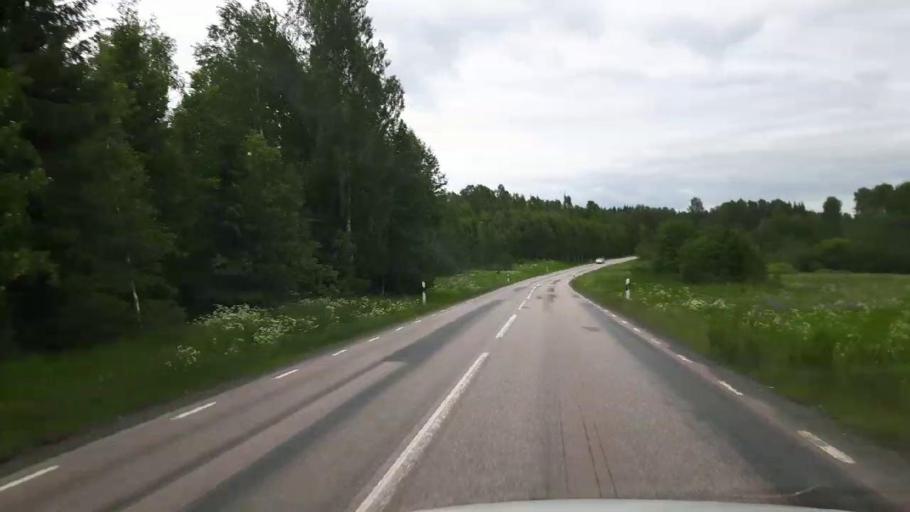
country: SE
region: Vaestmanland
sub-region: Kopings Kommun
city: Kolsva
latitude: 59.6154
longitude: 15.8250
